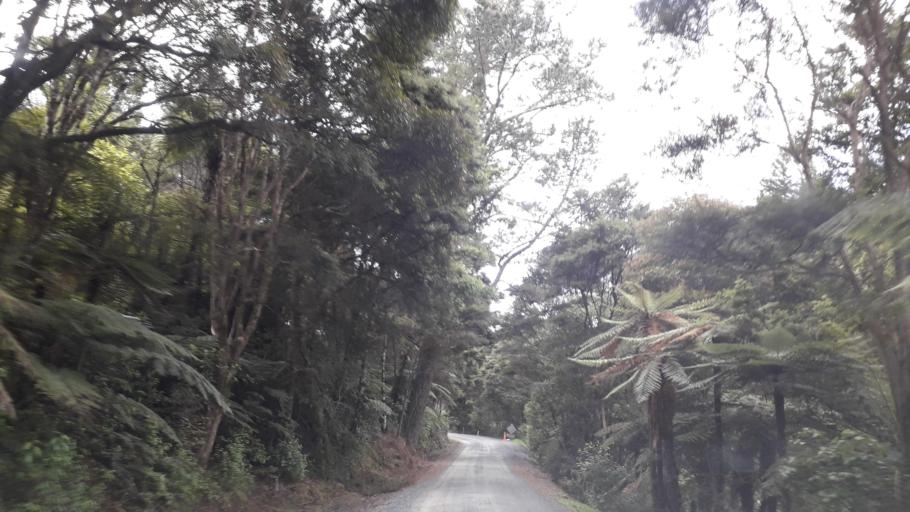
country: NZ
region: Northland
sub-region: Far North District
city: Taipa
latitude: -35.0564
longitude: 173.5535
